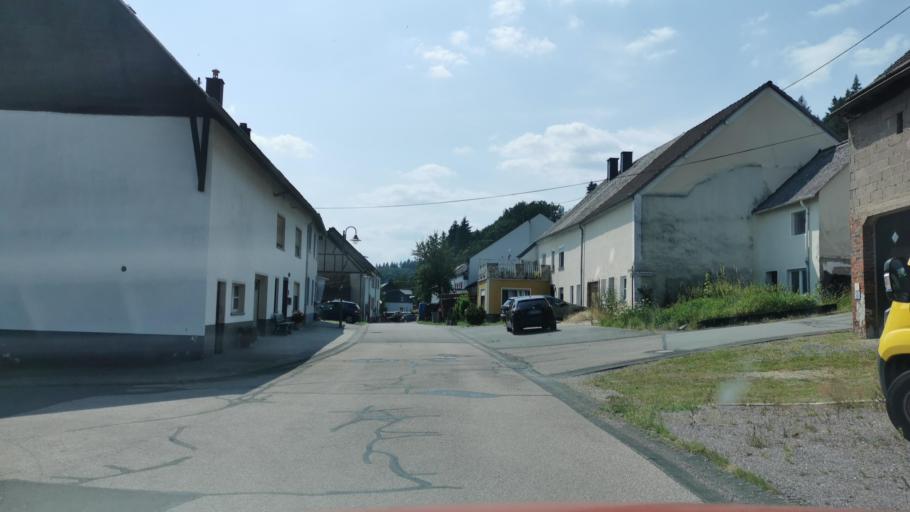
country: DE
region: Rheinland-Pfalz
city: Neunkirchen
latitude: 49.7495
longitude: 6.9407
